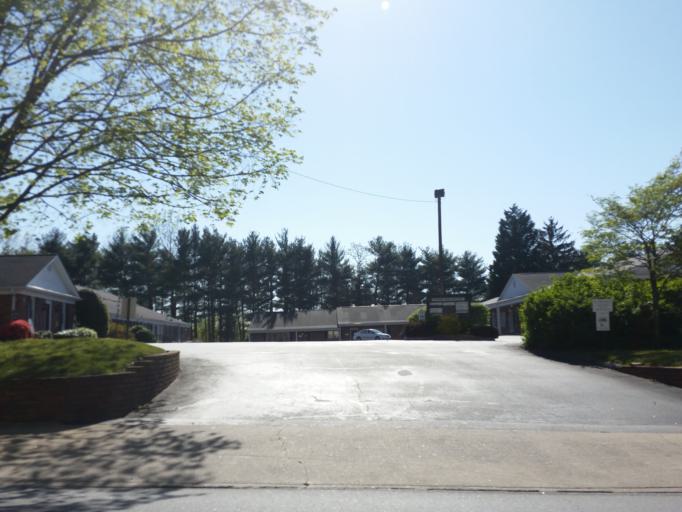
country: US
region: North Carolina
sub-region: Buncombe County
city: Asheville
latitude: 35.5811
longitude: -82.5509
